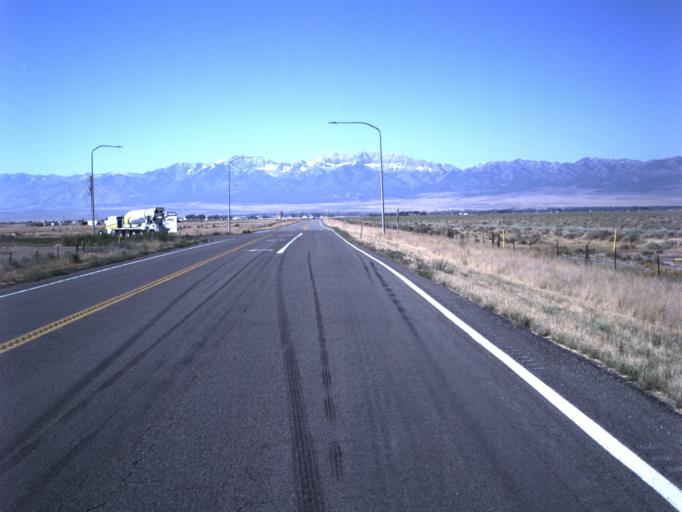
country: US
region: Utah
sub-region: Tooele County
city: Erda
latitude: 40.6150
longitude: -112.3700
